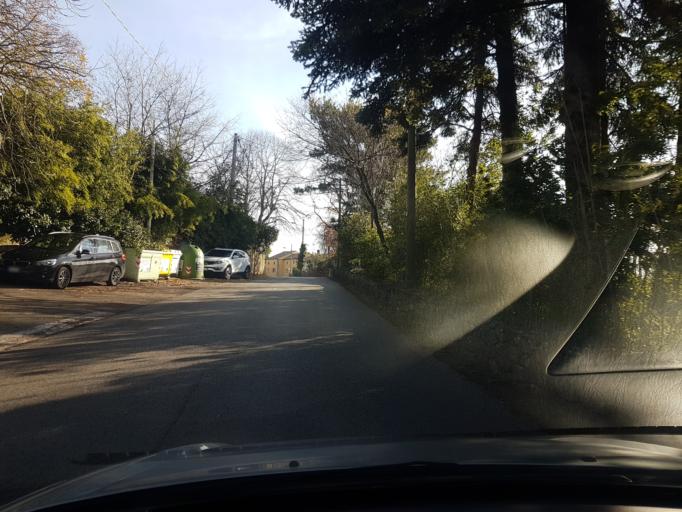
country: IT
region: Friuli Venezia Giulia
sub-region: Provincia di Trieste
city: Aurisina
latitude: 45.7768
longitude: 13.6838
